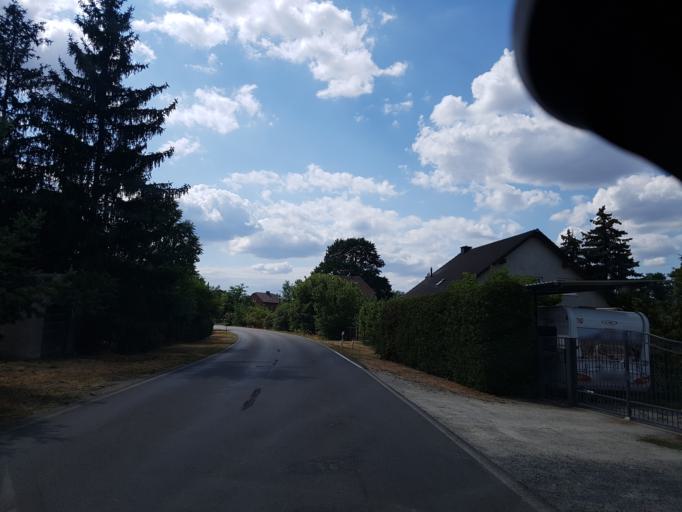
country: DE
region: Brandenburg
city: Cottbus
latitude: 51.7212
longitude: 14.3730
